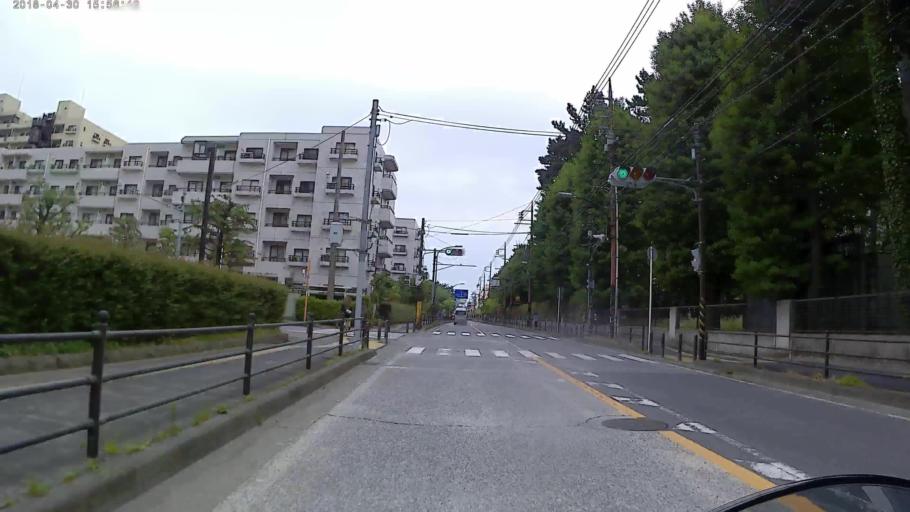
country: JP
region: Tokyo
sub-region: Machida-shi
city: Machida
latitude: 35.5339
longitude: 139.4305
